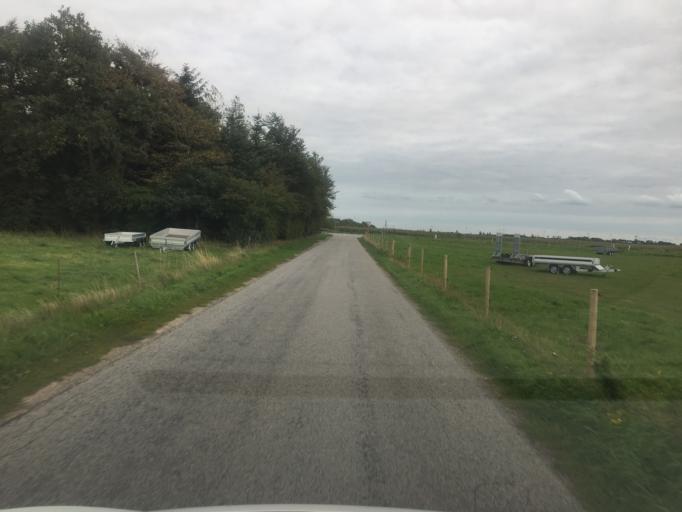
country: DK
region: South Denmark
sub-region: Tonder Kommune
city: Tonder
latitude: 54.9579
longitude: 8.9220
